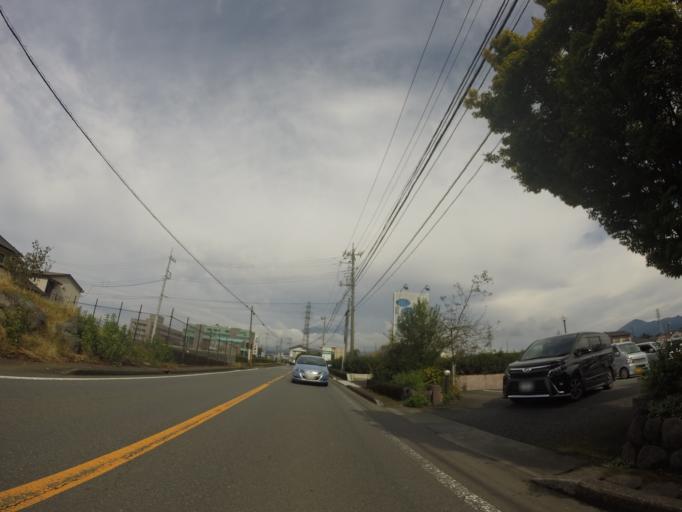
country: JP
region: Shizuoka
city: Fuji
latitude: 35.2034
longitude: 138.6842
